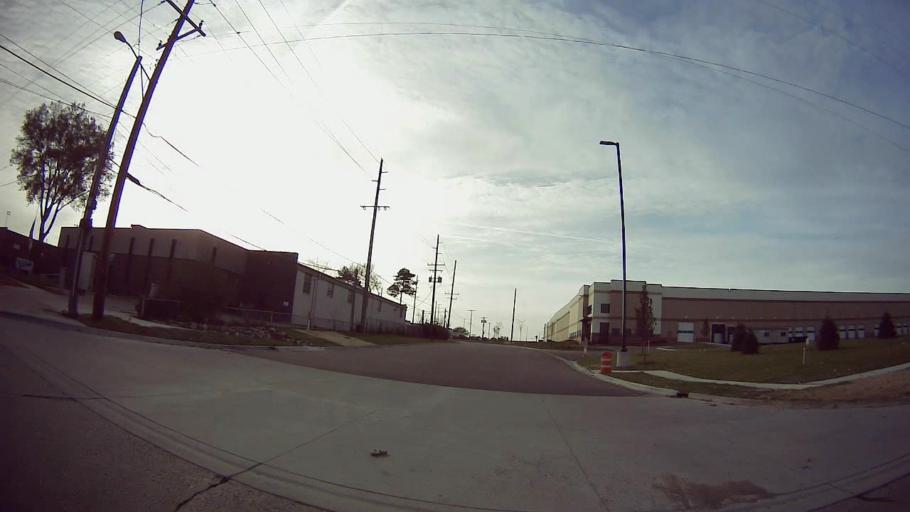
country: US
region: Michigan
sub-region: Oakland County
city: Madison Heights
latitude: 42.4762
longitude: -83.0899
